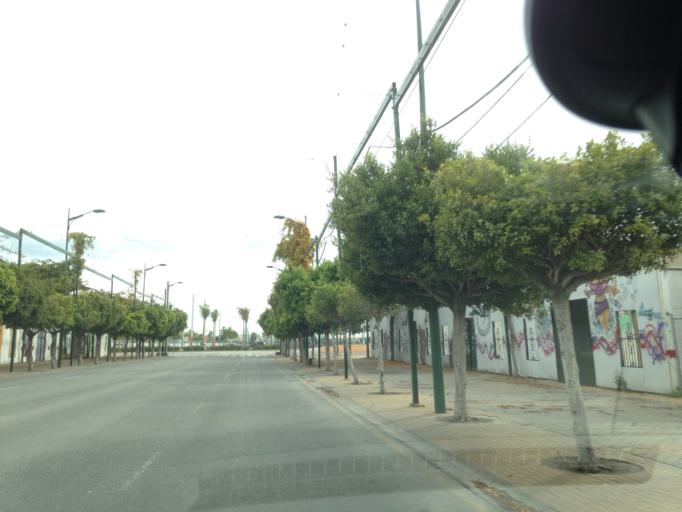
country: ES
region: Andalusia
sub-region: Provincia de Malaga
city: Malaga
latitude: 36.7023
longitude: -4.4627
